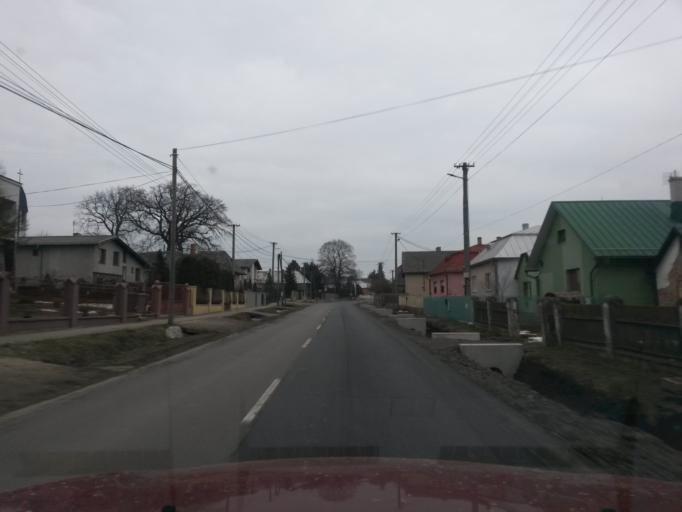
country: SK
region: Kosicky
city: Trebisov
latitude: 48.6849
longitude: 21.8129
